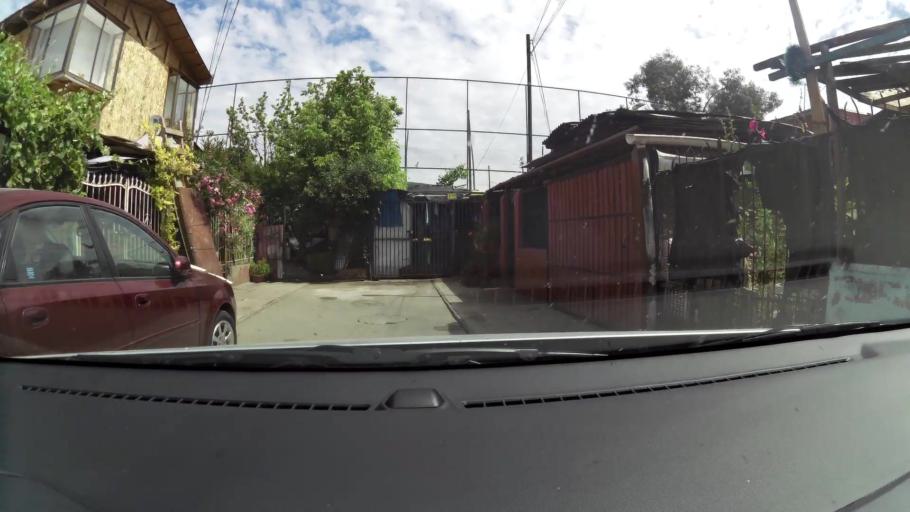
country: CL
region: Santiago Metropolitan
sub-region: Provincia de Santiago
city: La Pintana
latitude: -33.5791
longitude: -70.6589
